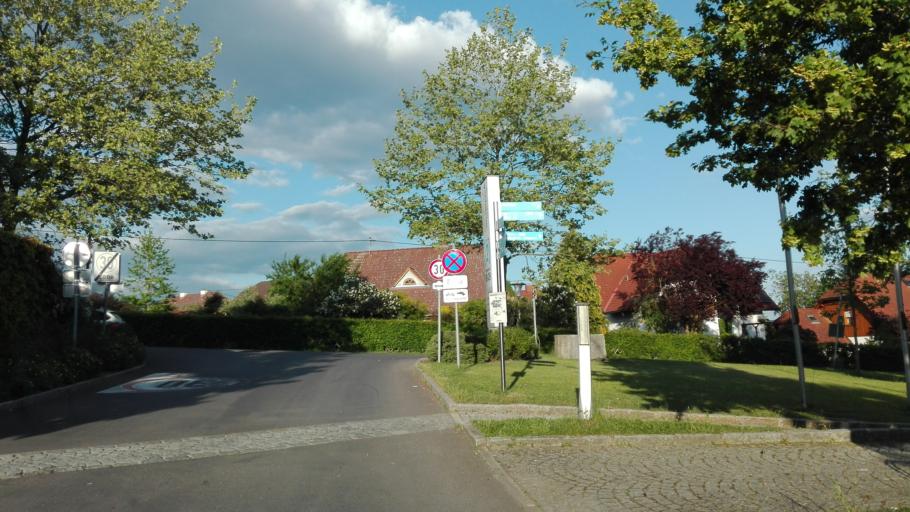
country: AT
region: Upper Austria
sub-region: Politischer Bezirk Urfahr-Umgebung
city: Engerwitzdorf
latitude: 48.3690
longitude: 14.5150
